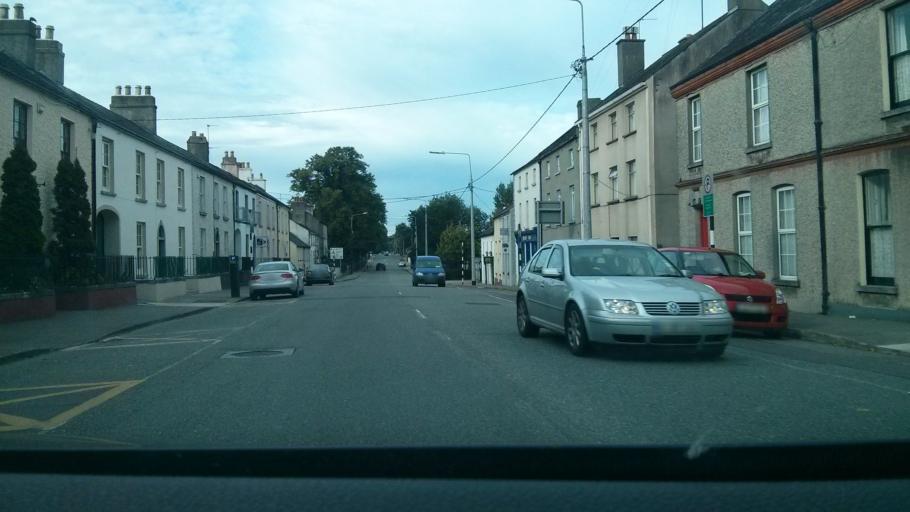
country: IE
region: Leinster
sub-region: Uibh Fhaili
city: Tullamore
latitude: 53.2718
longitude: -7.4950
